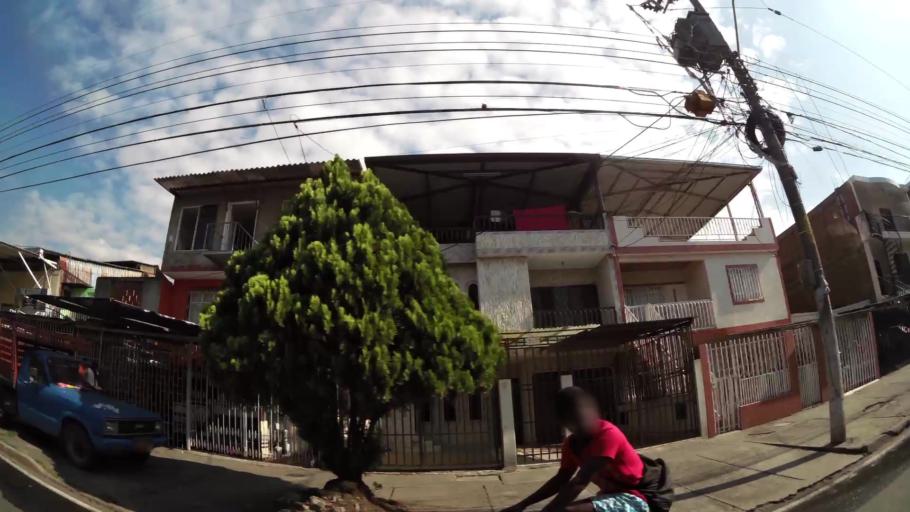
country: CO
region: Valle del Cauca
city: Cali
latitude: 3.4245
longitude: -76.5094
